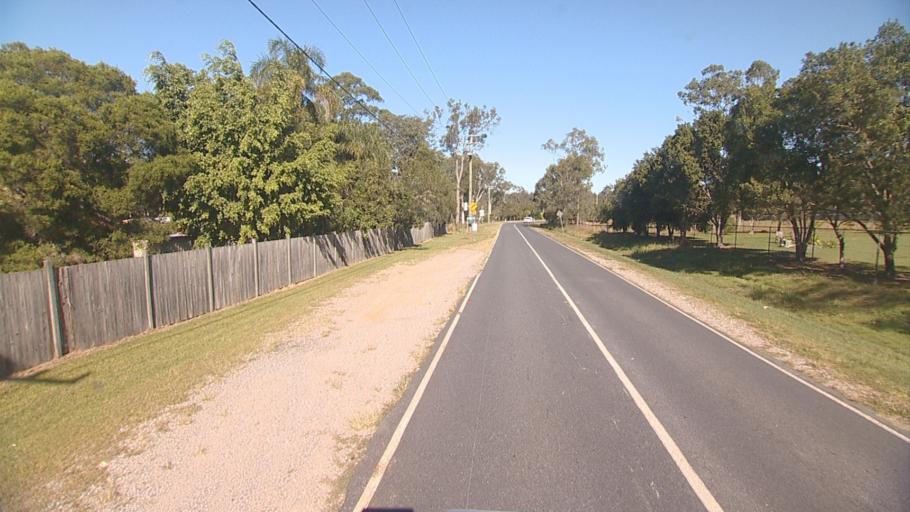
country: AU
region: Queensland
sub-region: Logan
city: Park Ridge South
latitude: -27.7193
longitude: 153.0590
